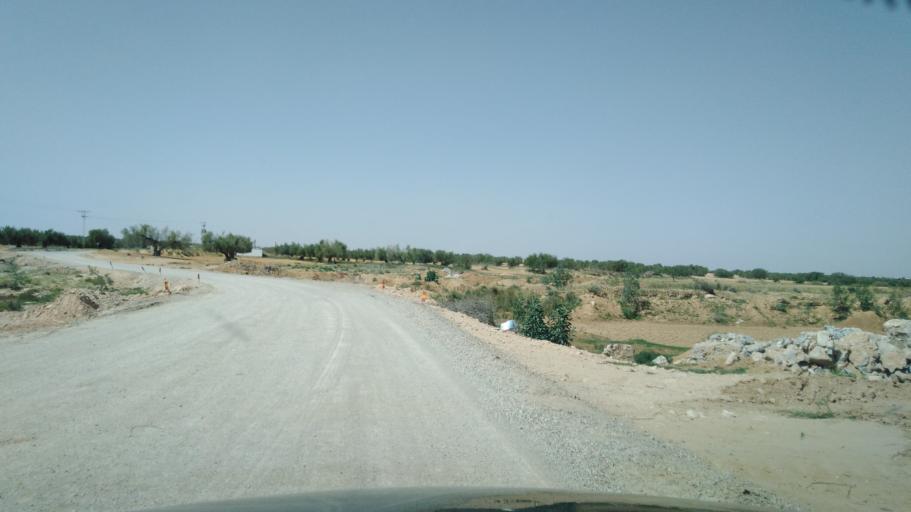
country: TN
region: Safaqis
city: Sfax
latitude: 34.6885
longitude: 10.4650
